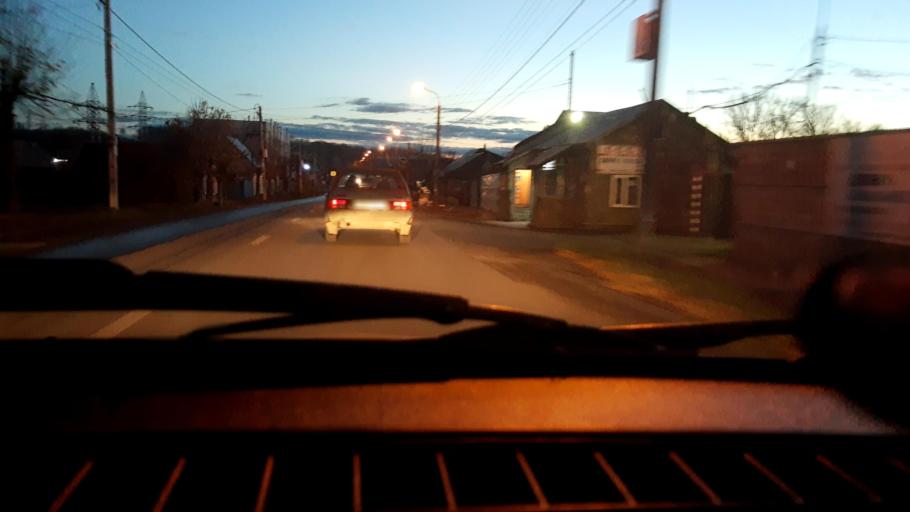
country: RU
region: Bashkortostan
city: Ufa
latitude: 54.7305
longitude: 55.9141
